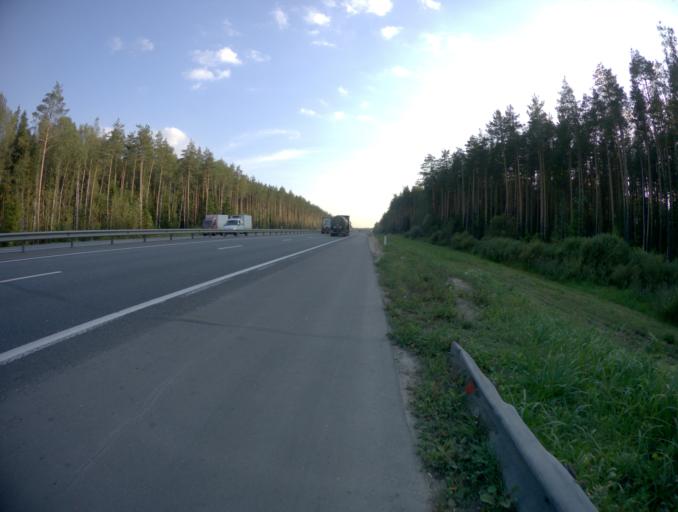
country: RU
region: Vladimir
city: Kameshkovo
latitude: 56.1880
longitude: 40.9495
